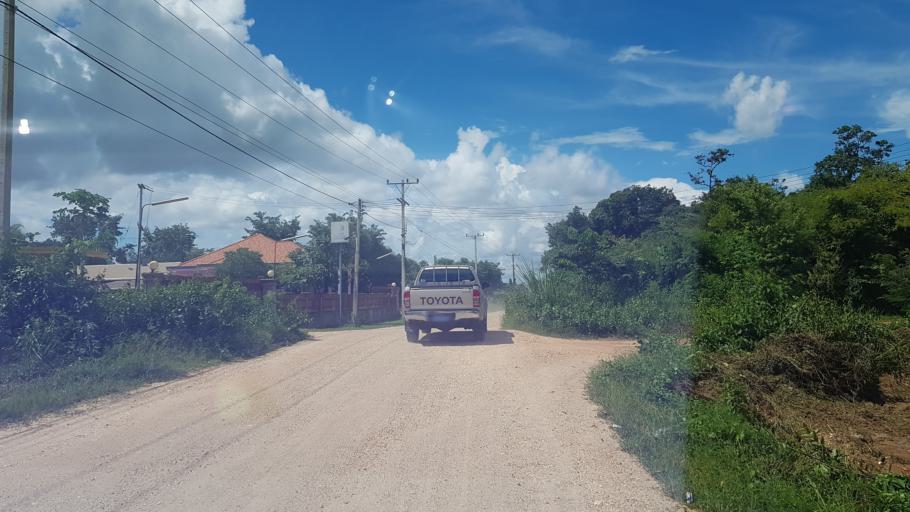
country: LA
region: Vientiane
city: Vientiane
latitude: 18.2236
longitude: 102.5185
